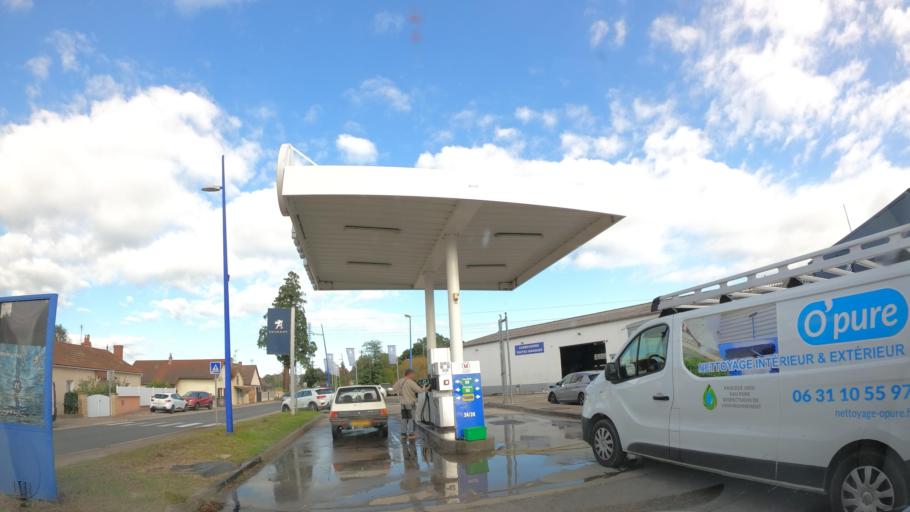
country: FR
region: Auvergne
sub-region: Departement de l'Allier
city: Dompierre-sur-Besbre
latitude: 46.5172
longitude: 3.6914
